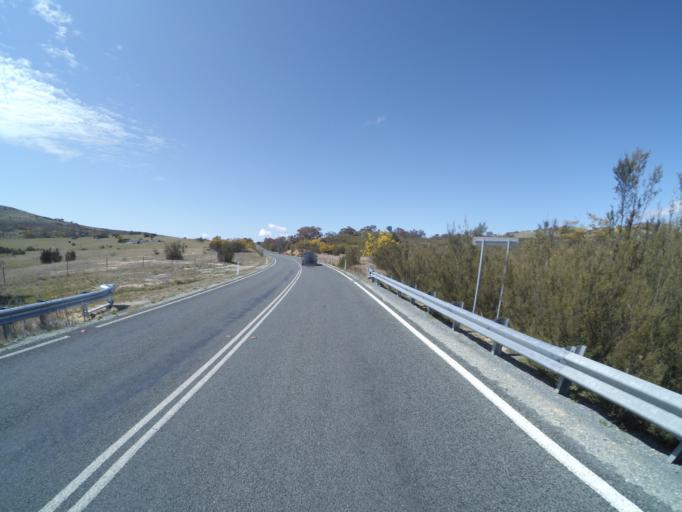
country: AU
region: Australian Capital Territory
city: Macarthur
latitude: -35.4562
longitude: 149.0095
